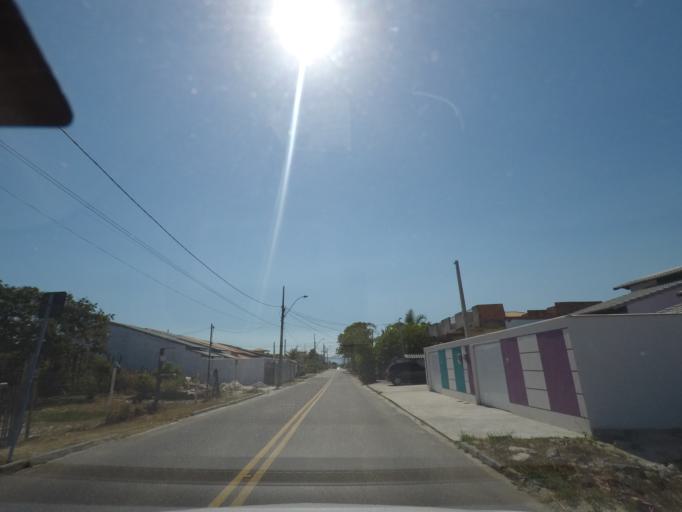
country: BR
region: Rio de Janeiro
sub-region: Marica
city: Marica
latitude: -22.9668
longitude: -42.9066
